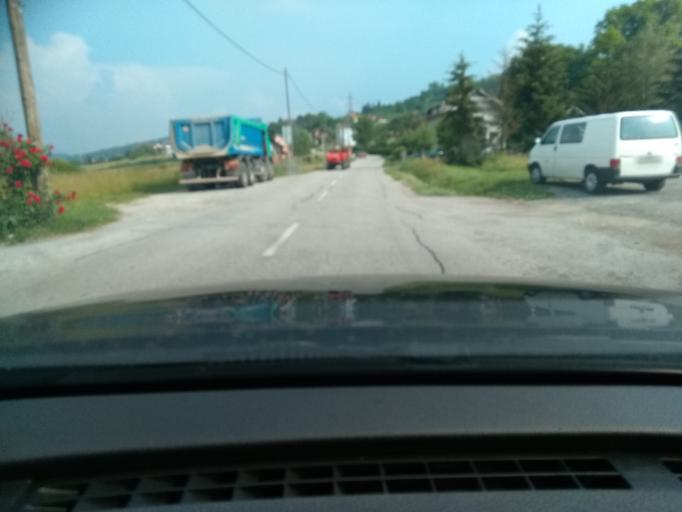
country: HR
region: Krapinsko-Zagorska
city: Pregrada
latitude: 46.0685
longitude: 15.7638
